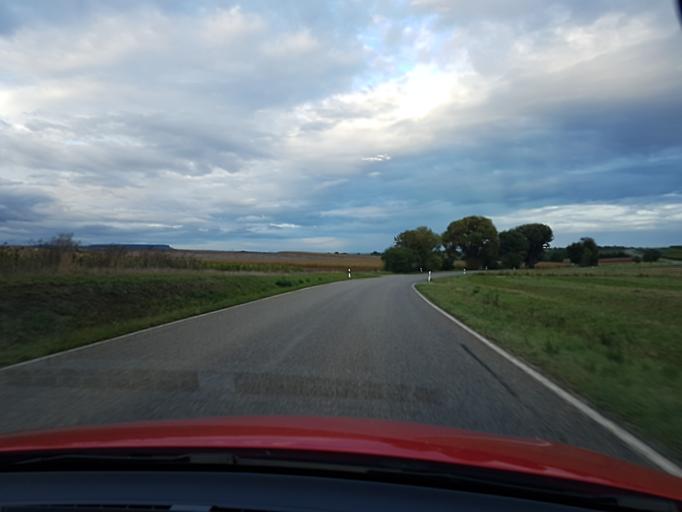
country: DE
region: Baden-Wuerttemberg
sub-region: Regierungsbezirk Stuttgart
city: Guglingen
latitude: 49.0518
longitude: 9.0123
